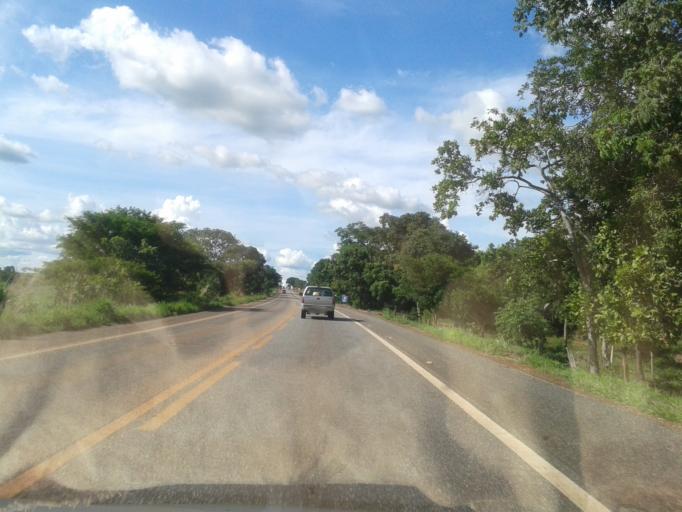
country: BR
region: Goias
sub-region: Mozarlandia
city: Mozarlandia
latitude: -14.7711
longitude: -50.5369
